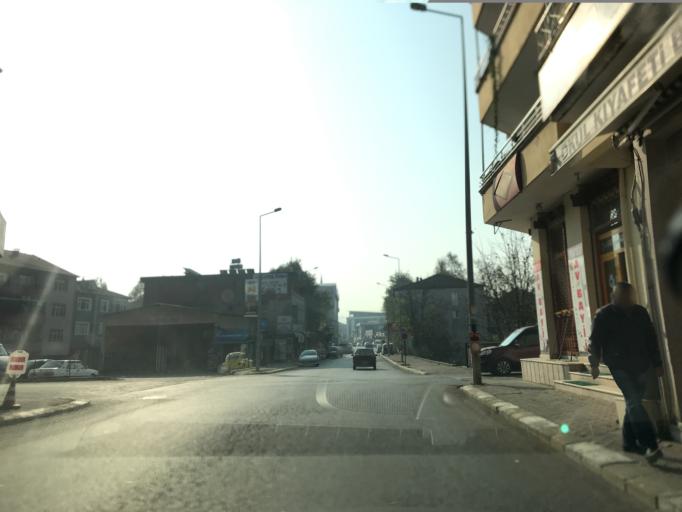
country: TR
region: Duzce
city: Cumayeri
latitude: 40.8761
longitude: 30.9502
